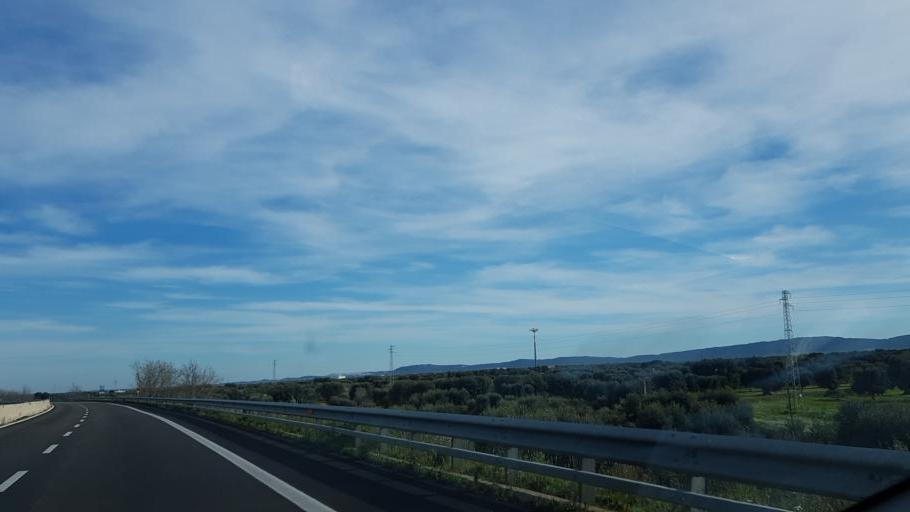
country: IT
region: Apulia
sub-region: Provincia di Brindisi
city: Montalbano
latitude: 40.8275
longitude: 17.4694
